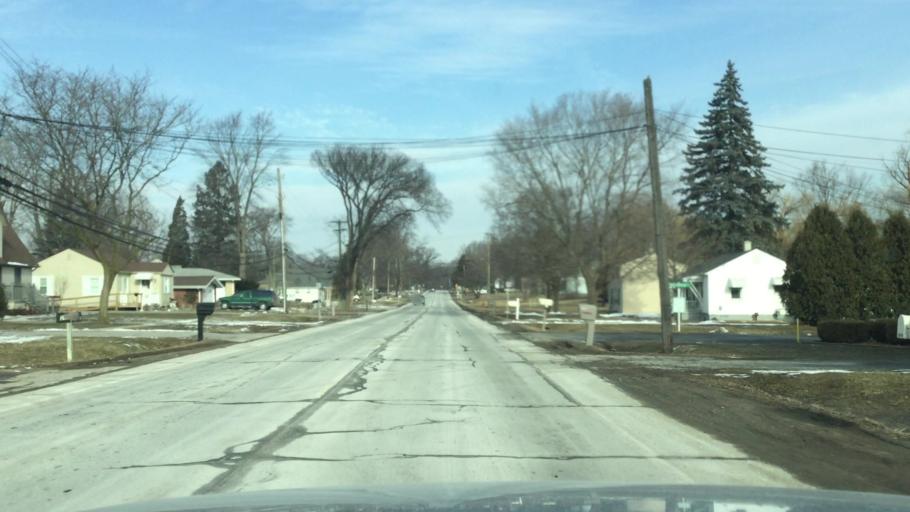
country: US
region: Michigan
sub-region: Wayne County
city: Flat Rock
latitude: 42.1017
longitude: -83.2961
